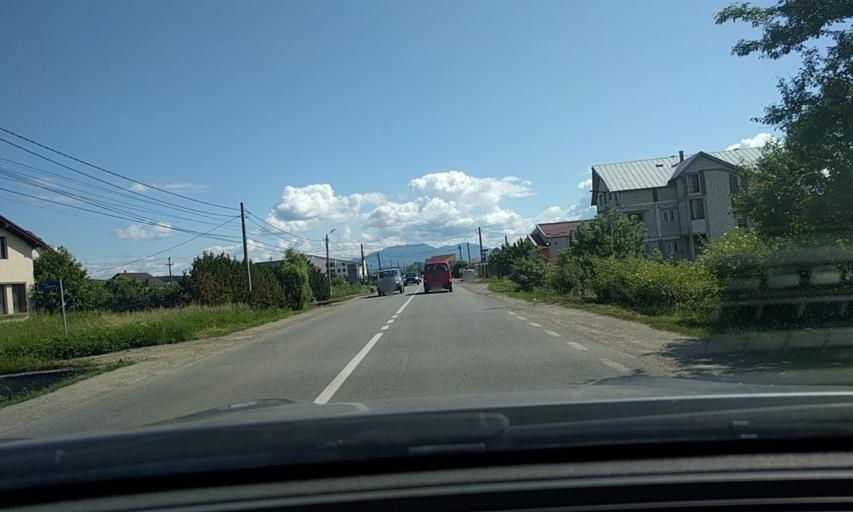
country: RO
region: Bistrita-Nasaud
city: Bistrita
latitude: 47.1522
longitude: 24.5048
